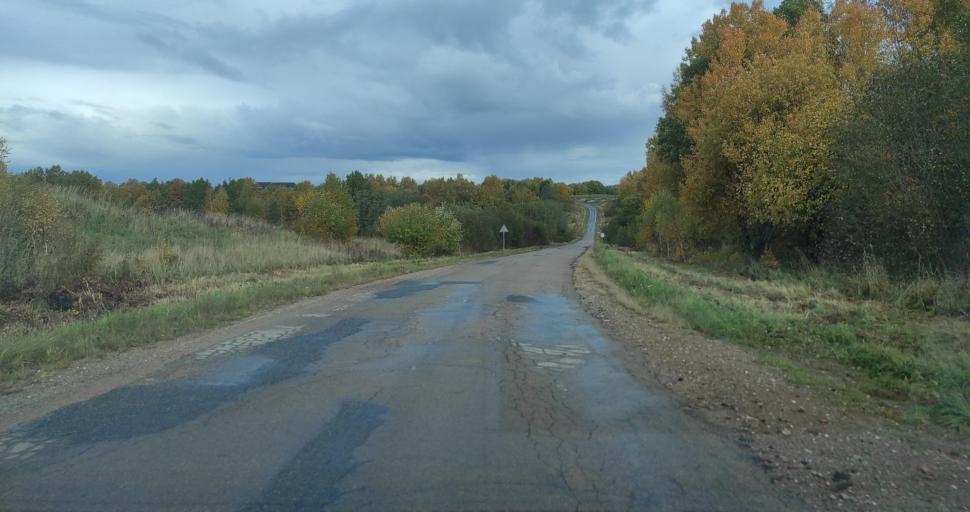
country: LV
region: Vainode
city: Vainode
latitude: 56.5604
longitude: 21.9063
